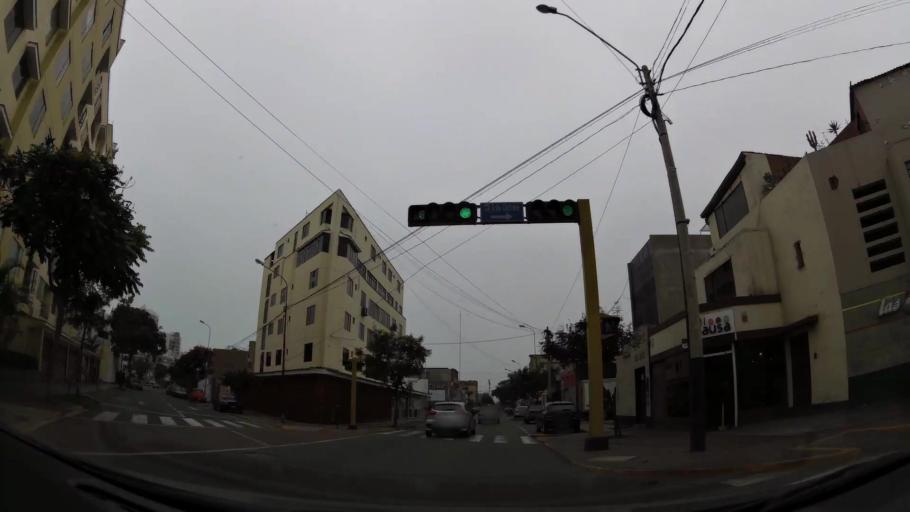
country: PE
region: Lima
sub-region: Lima
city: San Isidro
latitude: -12.1132
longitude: -77.0458
